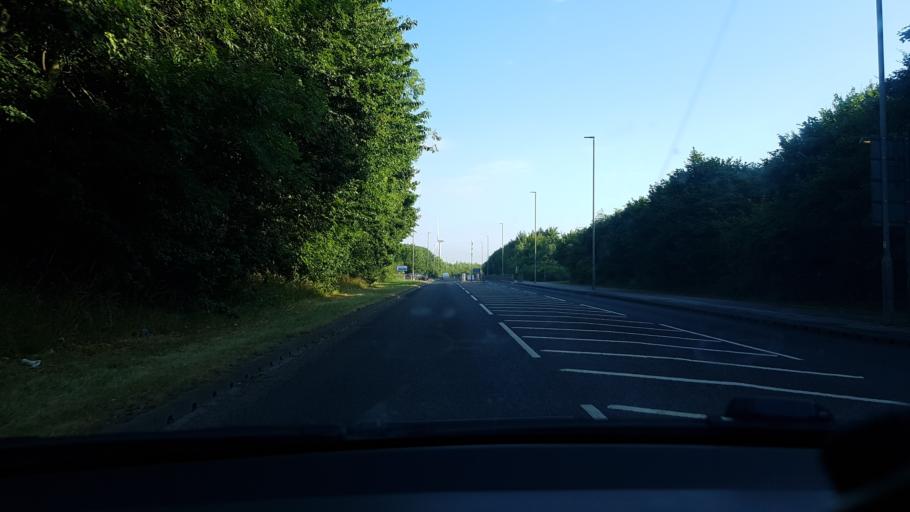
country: GB
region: England
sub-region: Nottinghamshire
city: Awsworth
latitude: 52.9849
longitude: -1.2911
